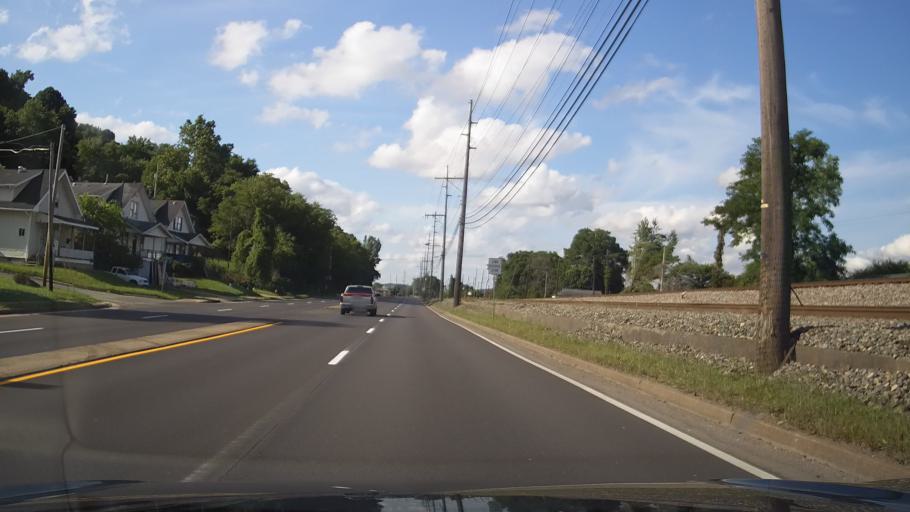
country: US
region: Kentucky
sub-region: Boyd County
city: Catlettsburg
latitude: 38.4078
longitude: -82.5999
